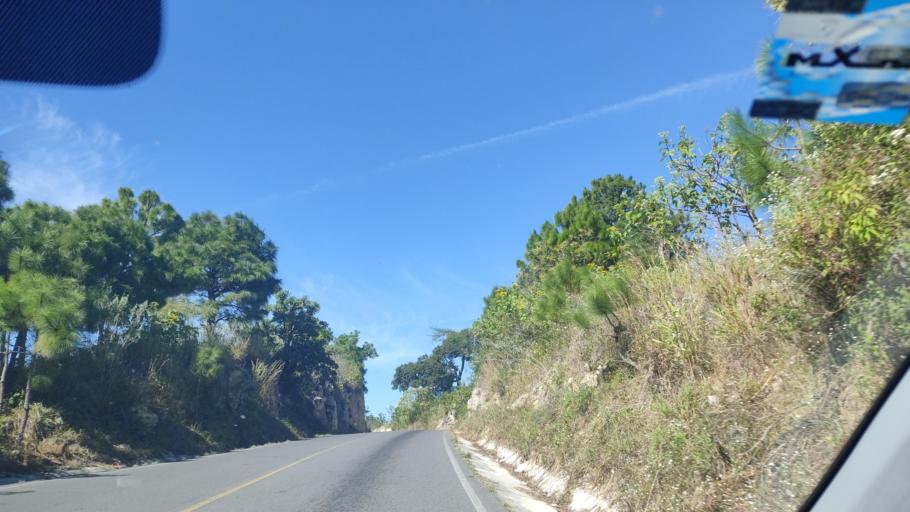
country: MX
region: Nayarit
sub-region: Jala
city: Rosa Blanca
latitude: 21.1005
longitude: -104.3639
